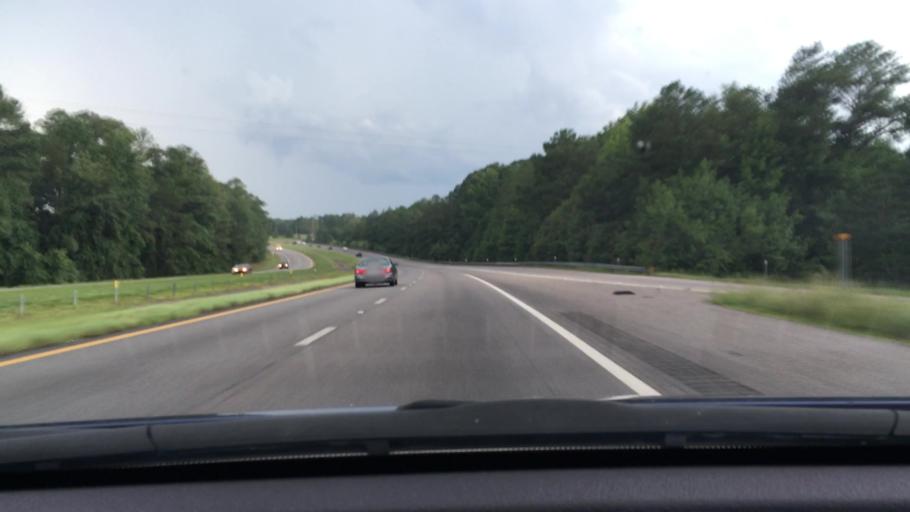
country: US
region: South Carolina
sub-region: Kershaw County
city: Lugoff
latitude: 34.1876
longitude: -80.6916
